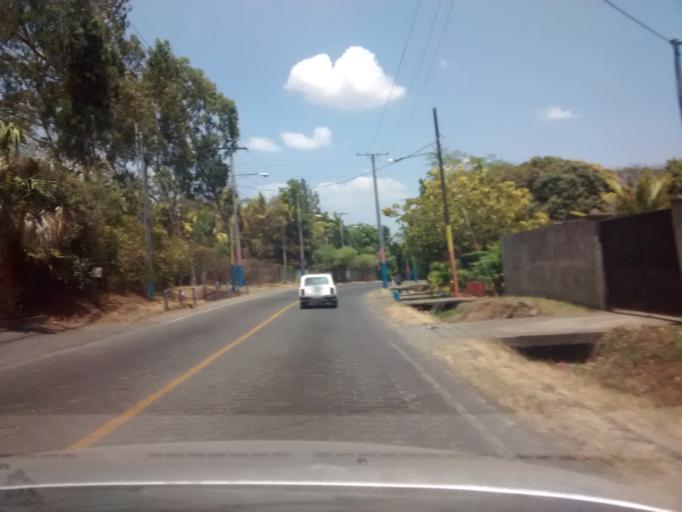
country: NI
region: Masaya
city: Ticuantepe
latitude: 12.0324
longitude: -86.2071
